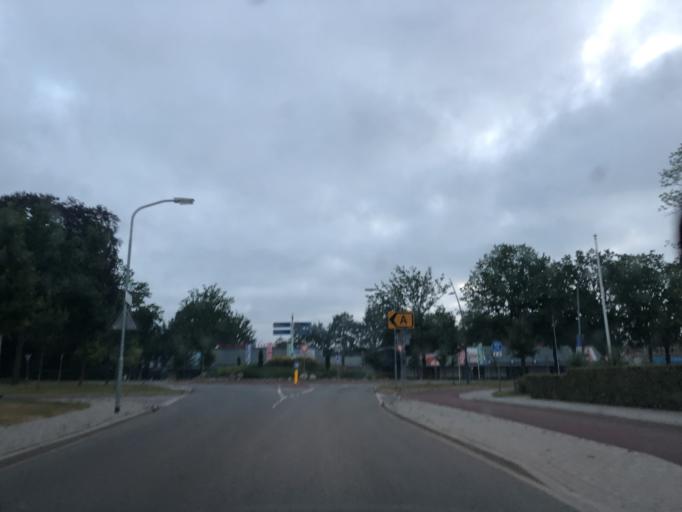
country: NL
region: Drenthe
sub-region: Gemeente Borger-Odoorn
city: Borger
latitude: 52.9237
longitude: 6.7961
